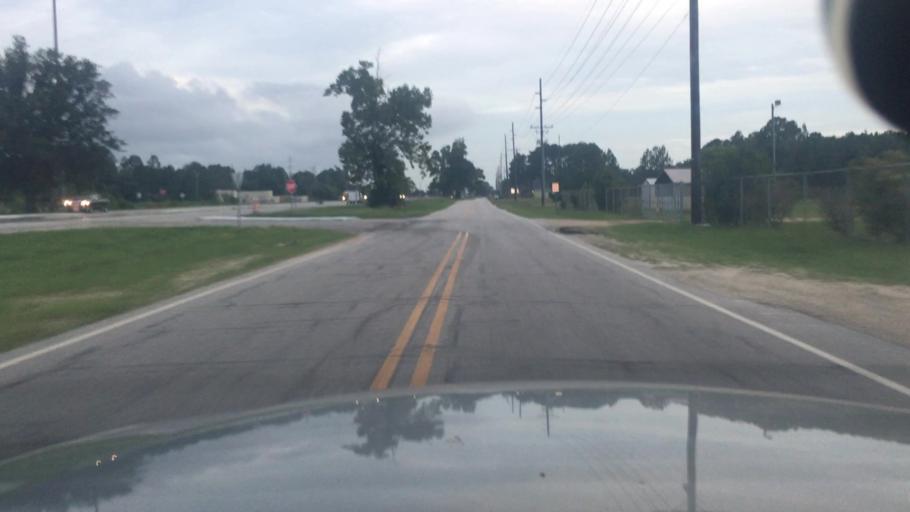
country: US
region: North Carolina
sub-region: Cumberland County
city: Hope Mills
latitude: 34.9820
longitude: -78.9070
